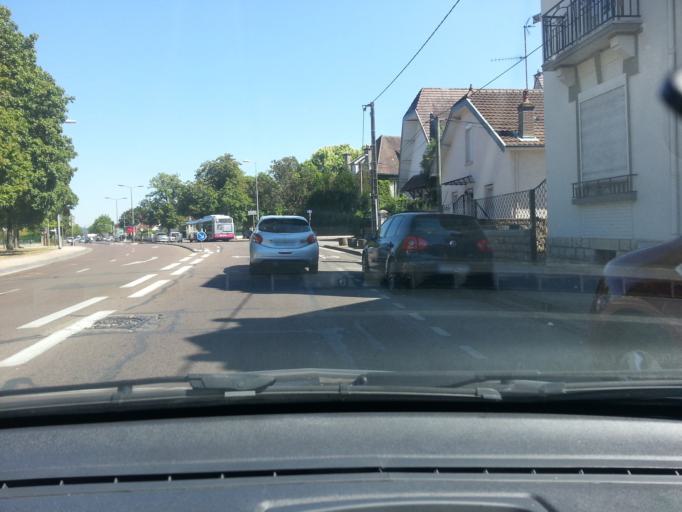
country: FR
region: Bourgogne
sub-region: Departement de la Cote-d'Or
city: Longvic
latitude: 47.3062
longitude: 5.0461
